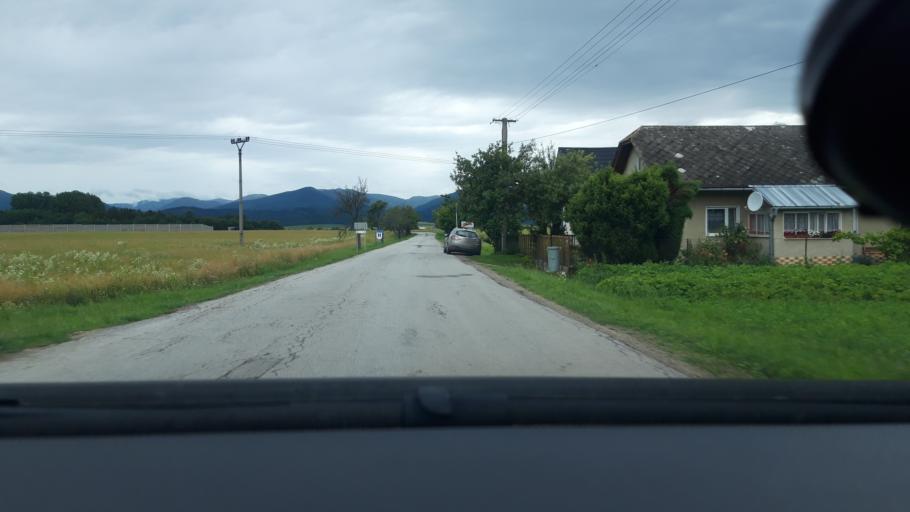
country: SK
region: Zilinsky
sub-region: Okres Martin
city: Martin
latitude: 48.9776
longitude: 18.9074
